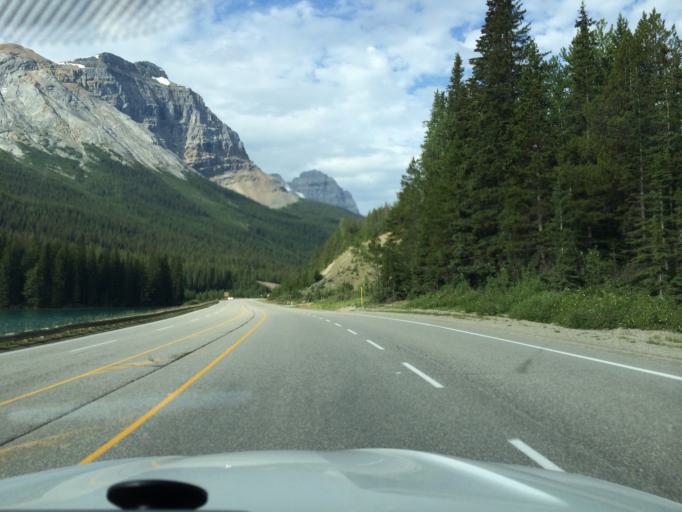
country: CA
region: Alberta
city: Lake Louise
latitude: 51.4404
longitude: -116.3542
